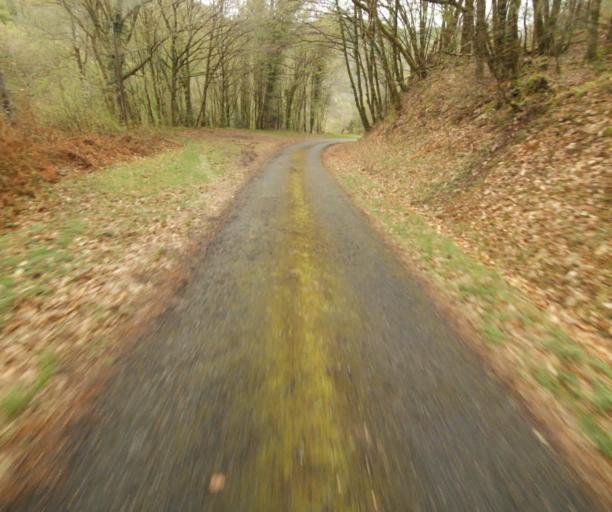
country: FR
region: Limousin
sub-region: Departement de la Correze
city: Saint-Privat
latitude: 45.2168
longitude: 2.0358
